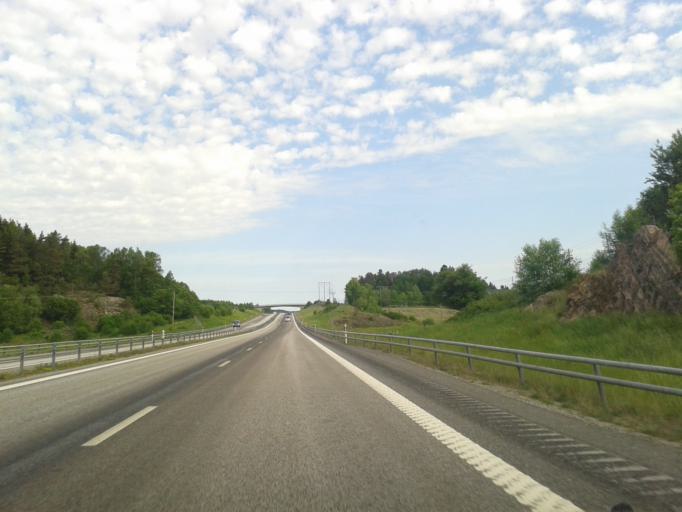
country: SE
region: Vaestra Goetaland
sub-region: Munkedals Kommun
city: Munkedal
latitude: 58.5025
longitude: 11.5657
